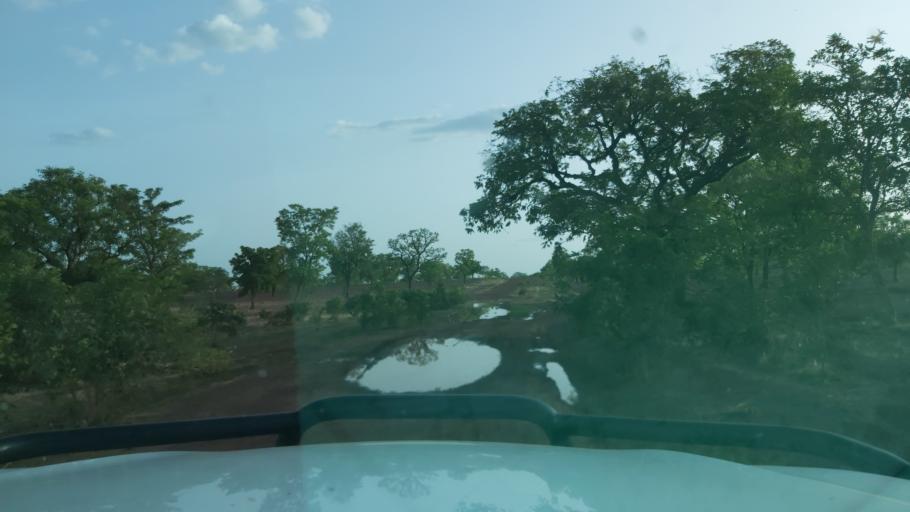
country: ML
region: Koulikoro
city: Kolokani
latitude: 13.2125
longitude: -7.9013
